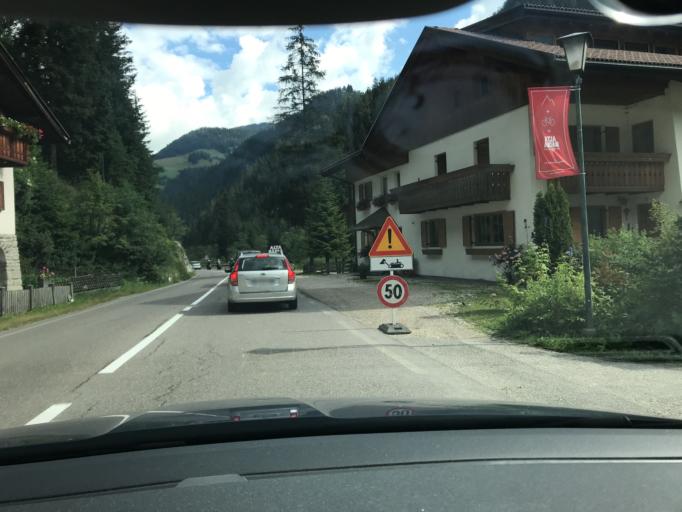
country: IT
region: Trentino-Alto Adige
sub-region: Bolzano
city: La Valle - Wengen
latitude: 46.6582
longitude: 11.9090
